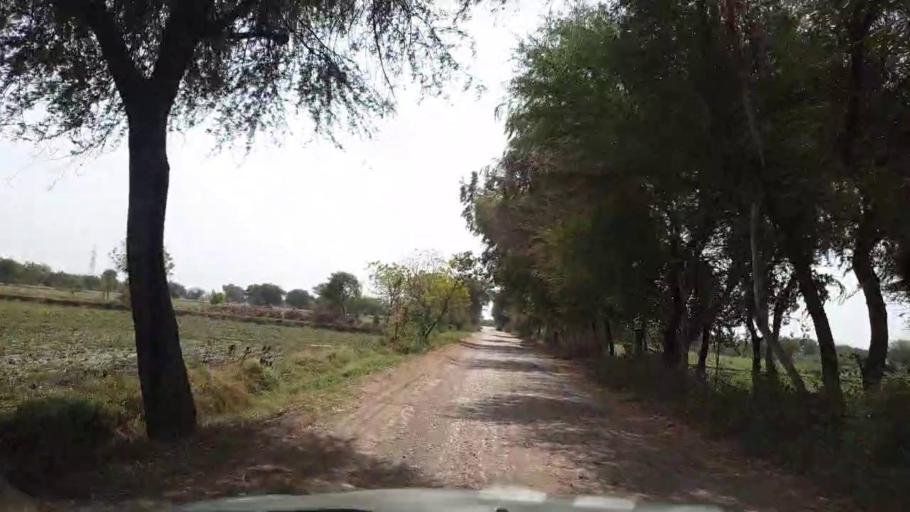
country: PK
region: Sindh
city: Matli
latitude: 25.0381
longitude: 68.7029
